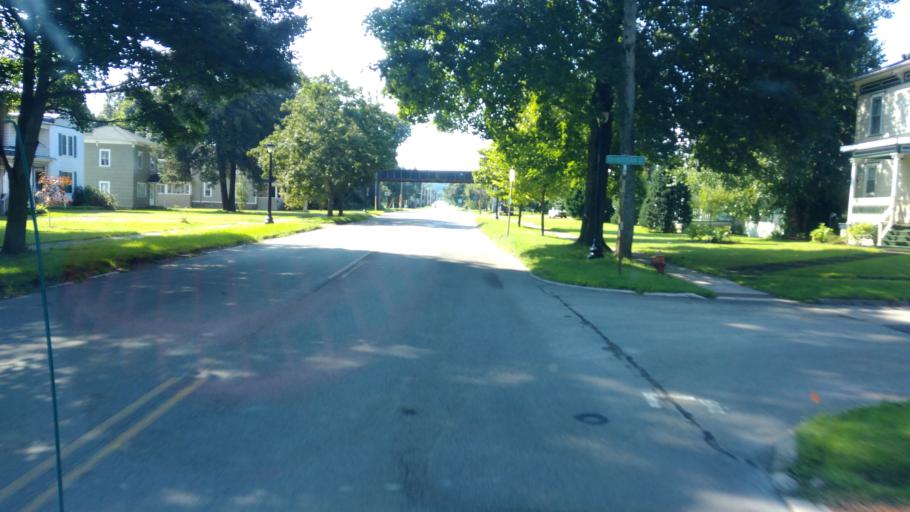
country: US
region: New York
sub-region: Allegany County
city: Cuba
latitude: 42.2128
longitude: -78.2753
